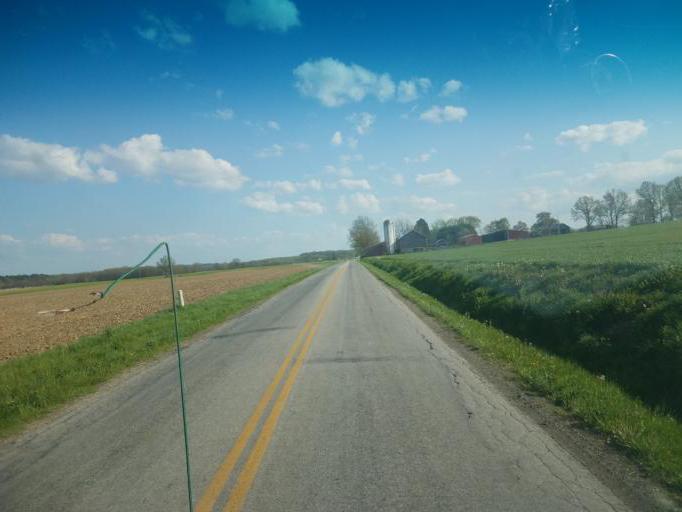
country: US
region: Ohio
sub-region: Wayne County
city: Apple Creek
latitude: 40.7771
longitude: -81.8803
